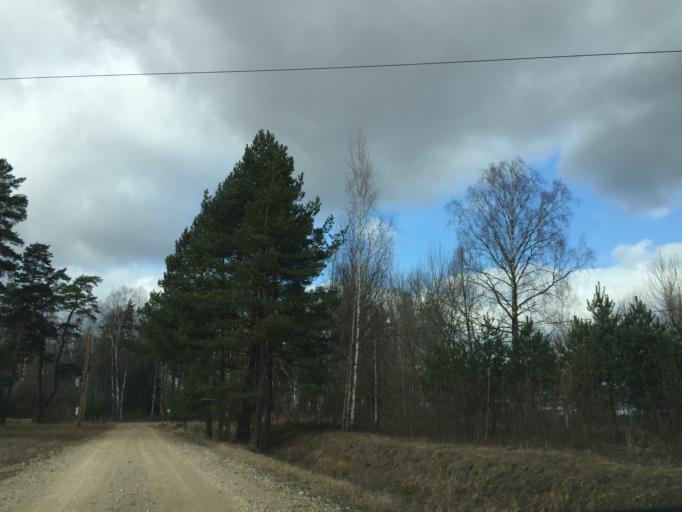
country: LV
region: Vecumnieki
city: Vecumnieki
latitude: 56.6010
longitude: 24.6256
